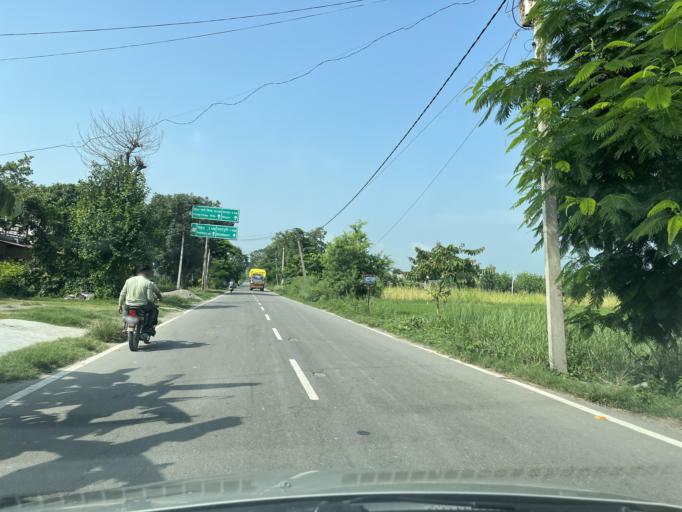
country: IN
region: Uttarakhand
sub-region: Udham Singh Nagar
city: Bazpur
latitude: 29.2035
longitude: 79.2071
